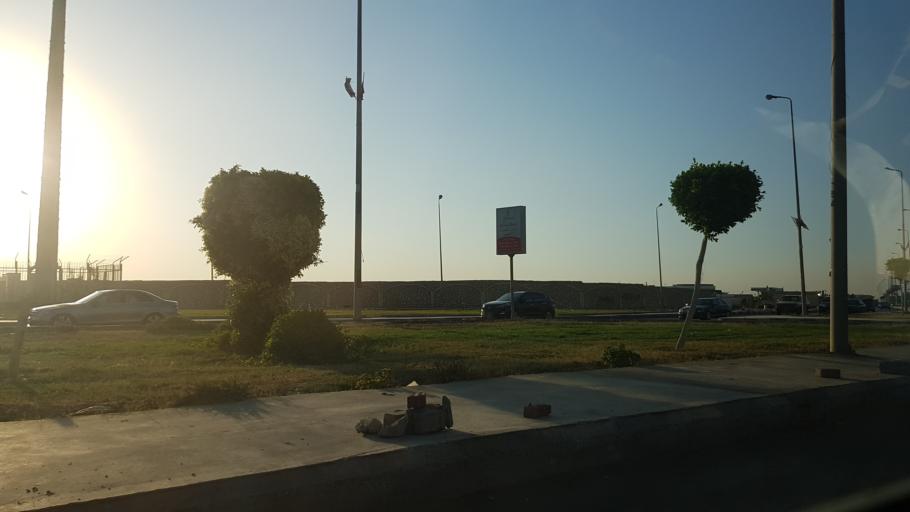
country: EG
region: Muhafazat al Qalyubiyah
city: Al Khankah
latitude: 30.0465
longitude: 31.4425
